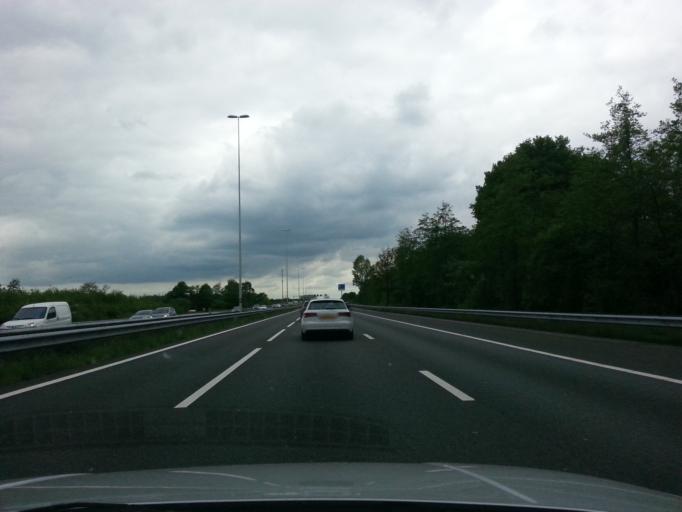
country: NL
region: Utrecht
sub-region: Gemeente Utrechtse Heuvelrug
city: Overberg
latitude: 52.0474
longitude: 5.4999
